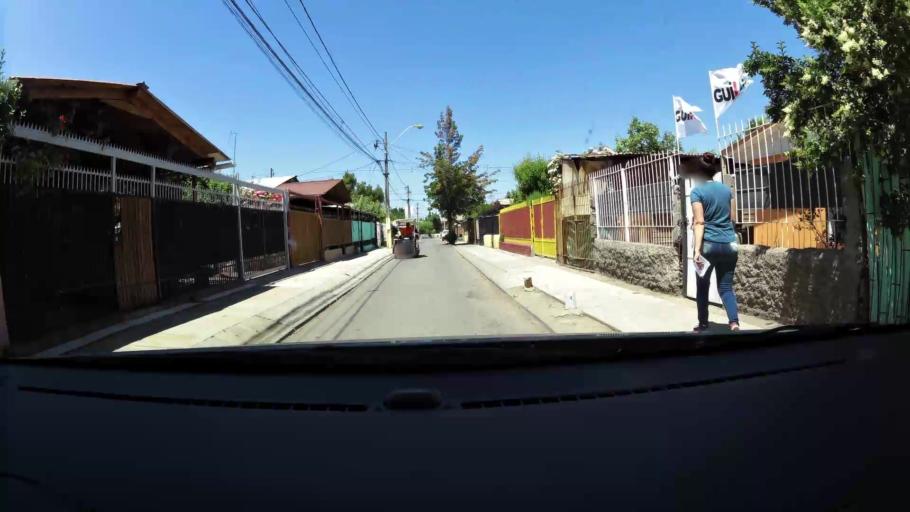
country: CL
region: Santiago Metropolitan
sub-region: Provincia de Santiago
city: La Pintana
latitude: -33.5712
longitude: -70.6653
